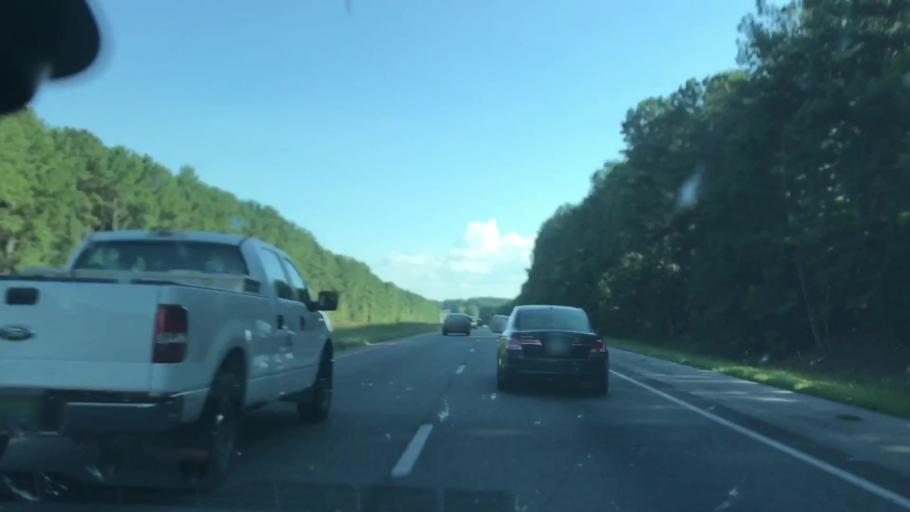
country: US
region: Georgia
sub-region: Harris County
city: Hamilton
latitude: 32.8053
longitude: -85.0215
